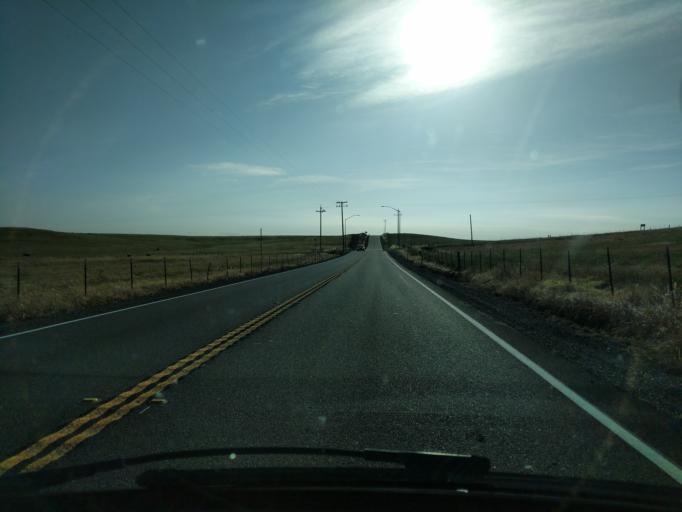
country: US
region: California
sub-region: Stanislaus County
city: East Oakdale
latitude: 37.9448
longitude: -120.8421
